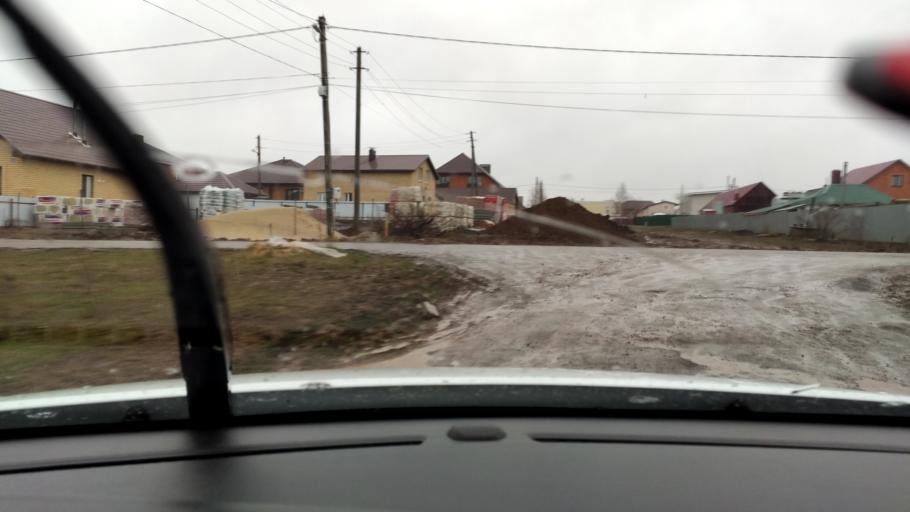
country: RU
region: Tatarstan
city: Vysokaya Gora
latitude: 55.9081
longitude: 49.3219
